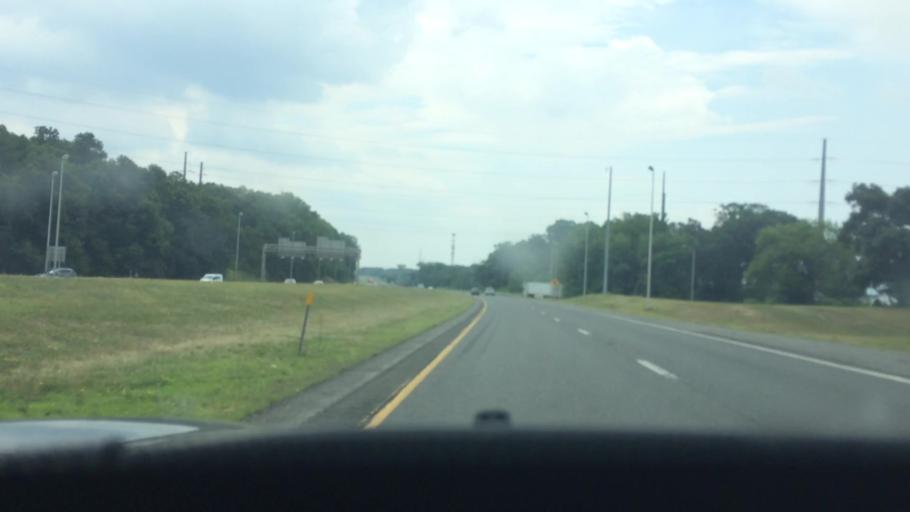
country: US
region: Massachusetts
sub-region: Hampden County
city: North Chicopee
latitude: 42.1614
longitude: -72.5412
